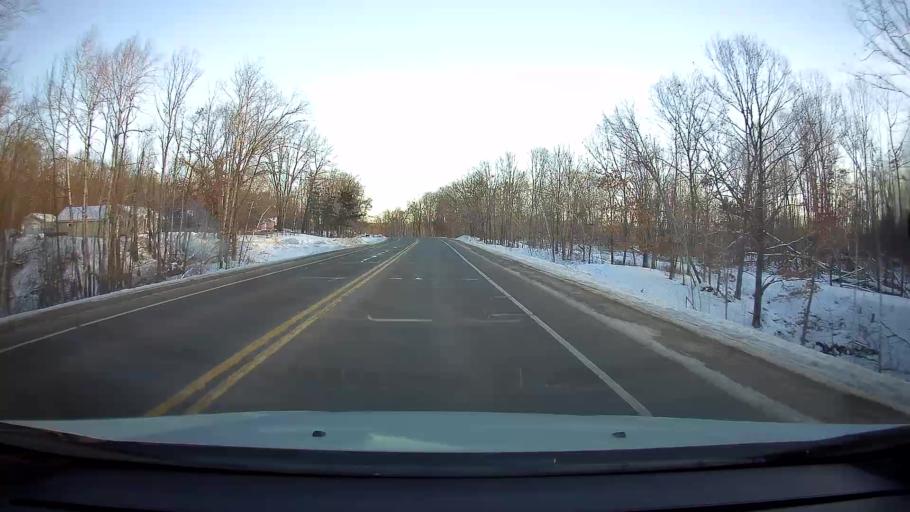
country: US
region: Wisconsin
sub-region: Barron County
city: Turtle Lake
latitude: 45.4133
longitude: -92.1340
